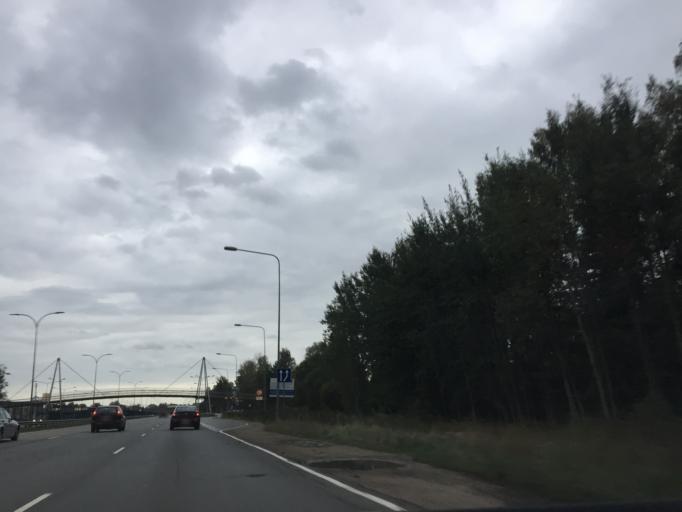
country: LV
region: Marupe
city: Marupe
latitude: 56.9421
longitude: 23.9972
